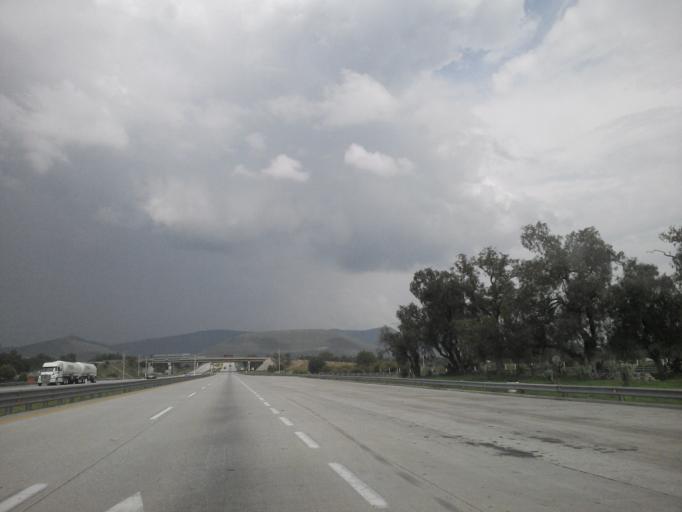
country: MX
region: Hidalgo
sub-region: Atitalaquia
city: Atitalaquia
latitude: 20.0658
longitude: -99.2177
